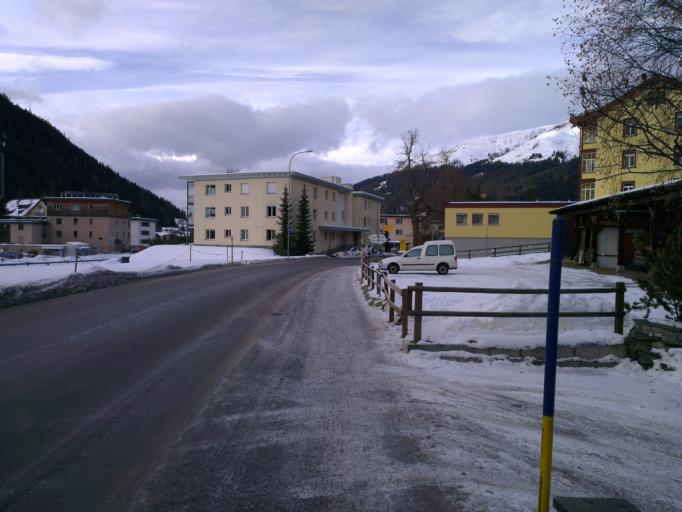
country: CH
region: Grisons
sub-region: Praettigau/Davos District
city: Davos
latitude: 46.8010
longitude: 9.8360
